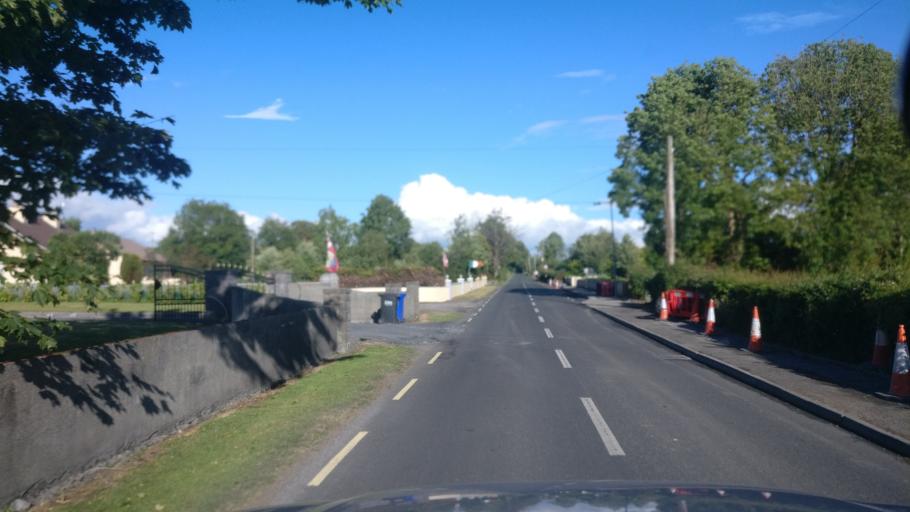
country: IE
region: Connaught
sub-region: County Galway
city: Ballinasloe
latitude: 53.2343
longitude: -8.2635
